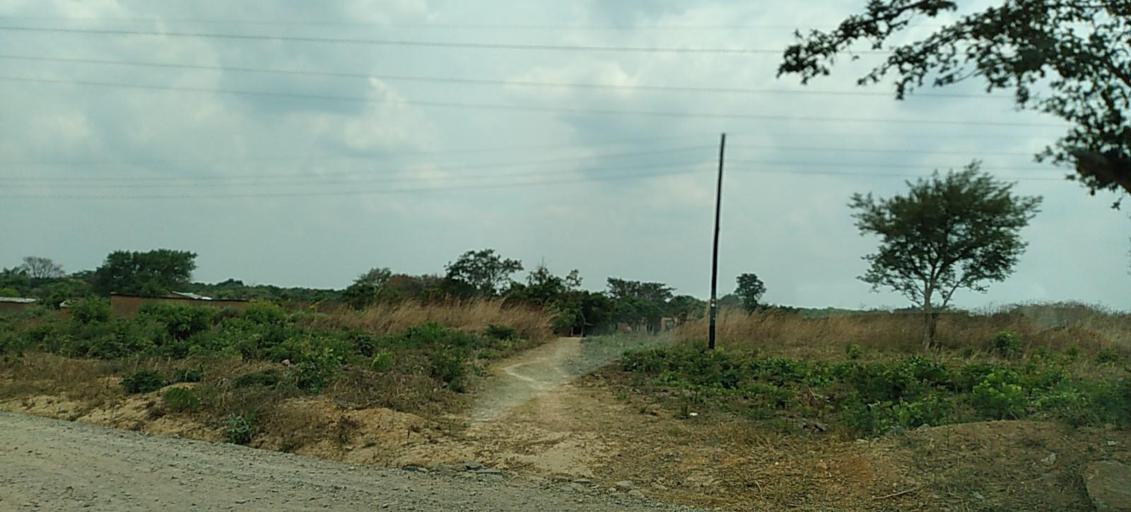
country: ZM
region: Copperbelt
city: Chililabombwe
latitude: -12.3136
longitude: 27.7898
